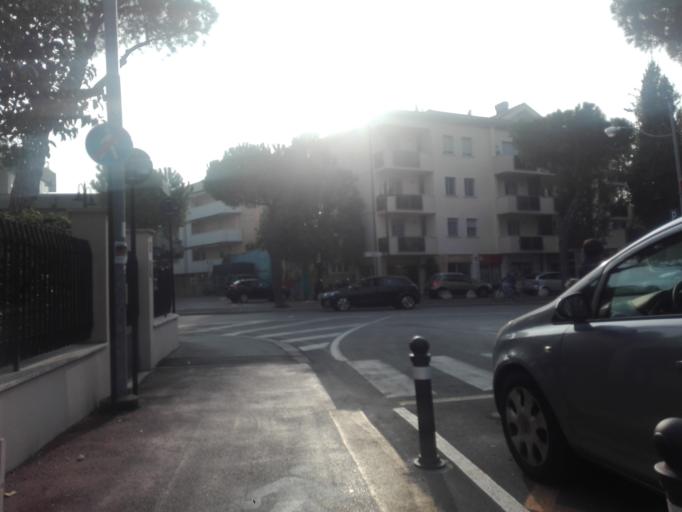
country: IT
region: Emilia-Romagna
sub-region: Provincia di Rimini
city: Rimini
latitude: 44.0656
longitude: 12.5617
